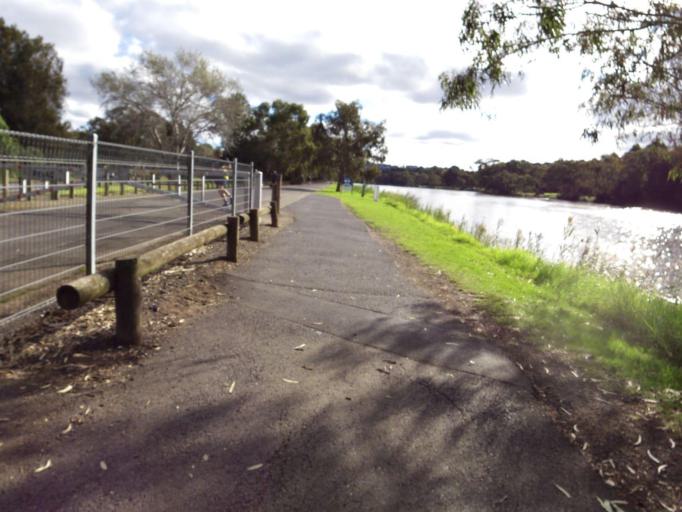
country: AU
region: Victoria
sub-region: Greater Geelong
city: Geelong
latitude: -38.1644
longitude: 144.3465
